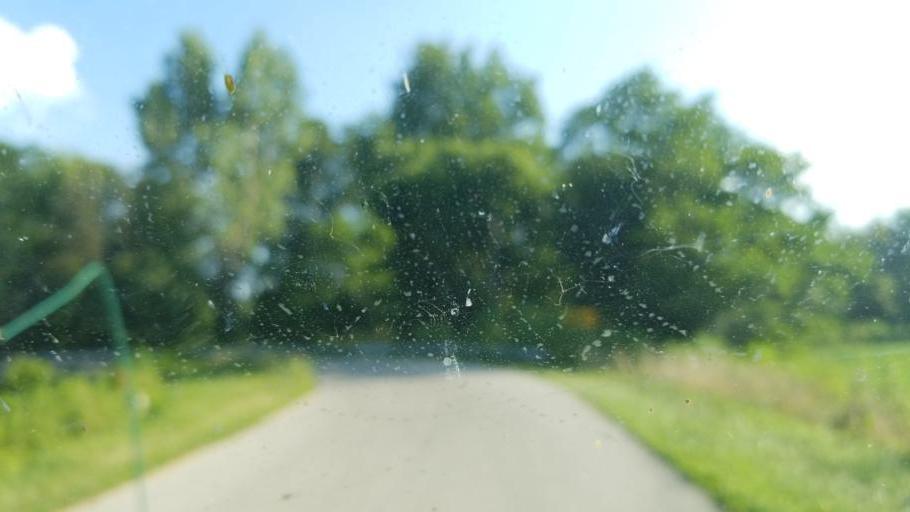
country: US
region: Ohio
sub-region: Crawford County
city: Bucyrus
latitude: 40.8325
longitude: -82.8984
